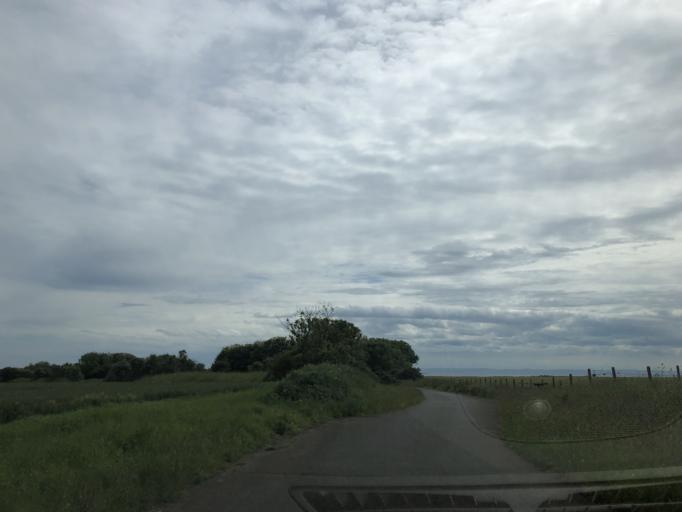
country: GB
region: Scotland
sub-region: Fife
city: Anstruther
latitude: 56.2728
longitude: -2.6004
